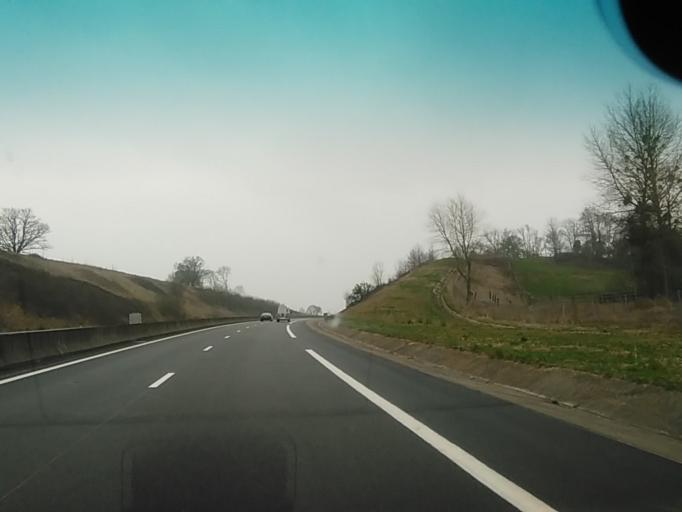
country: FR
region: Lower Normandy
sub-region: Departement de l'Orne
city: Gace
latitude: 48.7364
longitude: 0.2637
